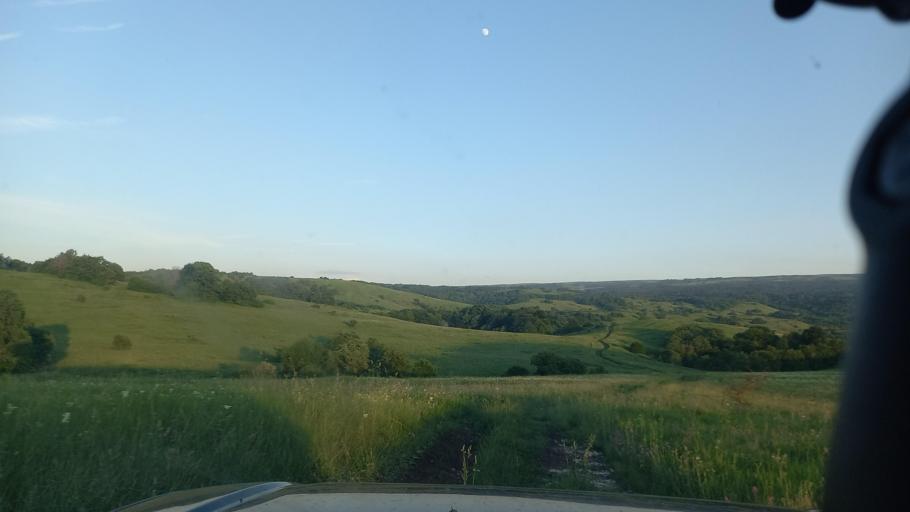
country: RU
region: Karachayevo-Cherkesiya
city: Pregradnaya
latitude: 44.1183
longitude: 41.1177
